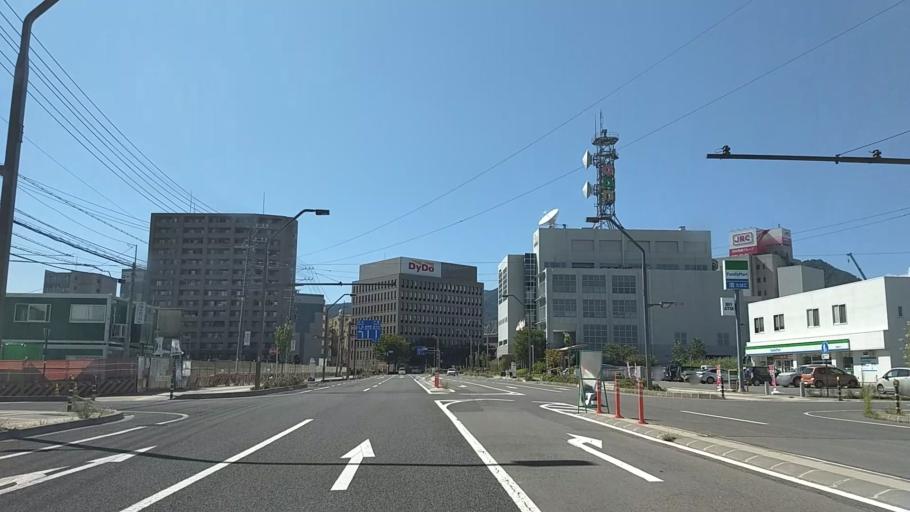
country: JP
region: Nagano
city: Nagano-shi
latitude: 36.6419
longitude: 138.1936
